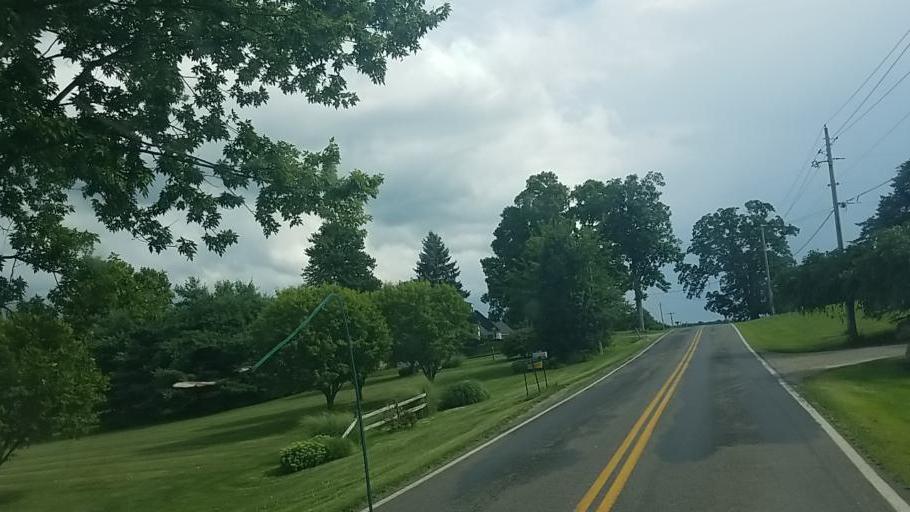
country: US
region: Ohio
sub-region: Medina County
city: Westfield Center
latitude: 41.0114
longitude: -81.9109
